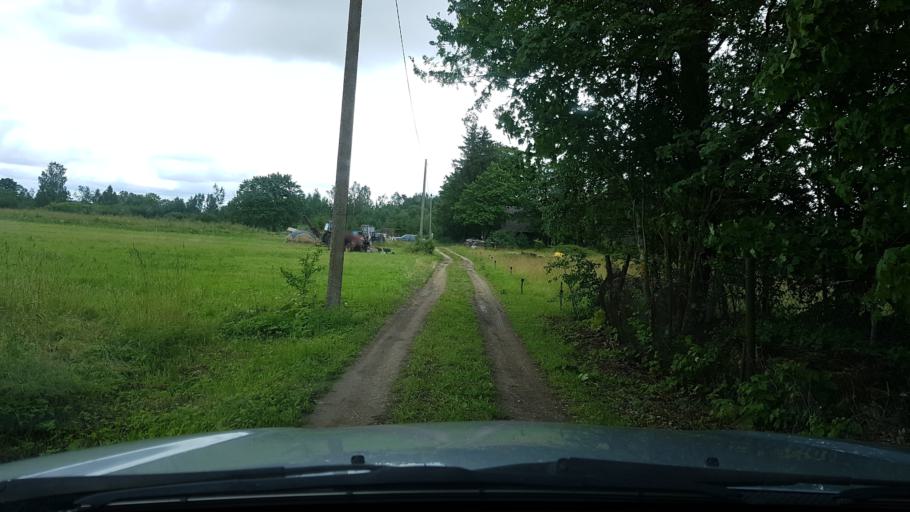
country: EE
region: Ida-Virumaa
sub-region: Sillamaee linn
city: Sillamae
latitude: 59.3685
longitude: 27.7519
